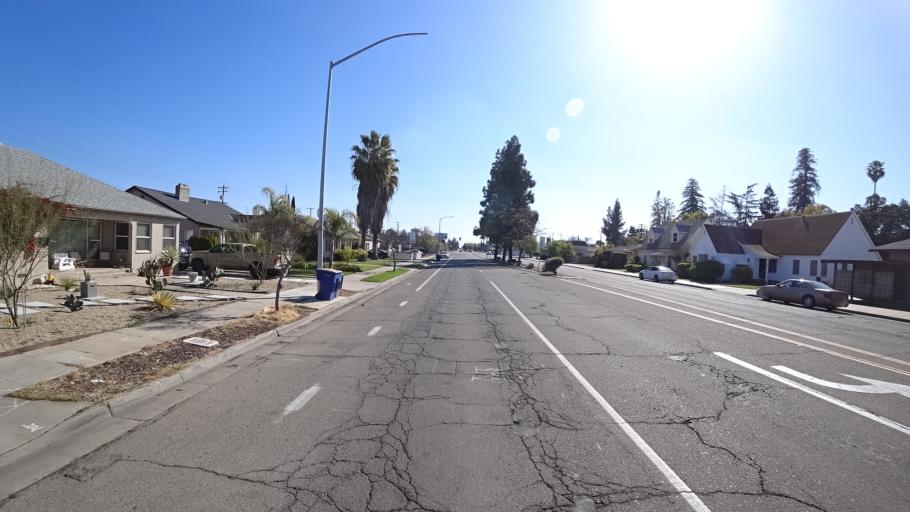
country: US
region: California
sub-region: Fresno County
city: Fresno
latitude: 36.7795
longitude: -119.8106
